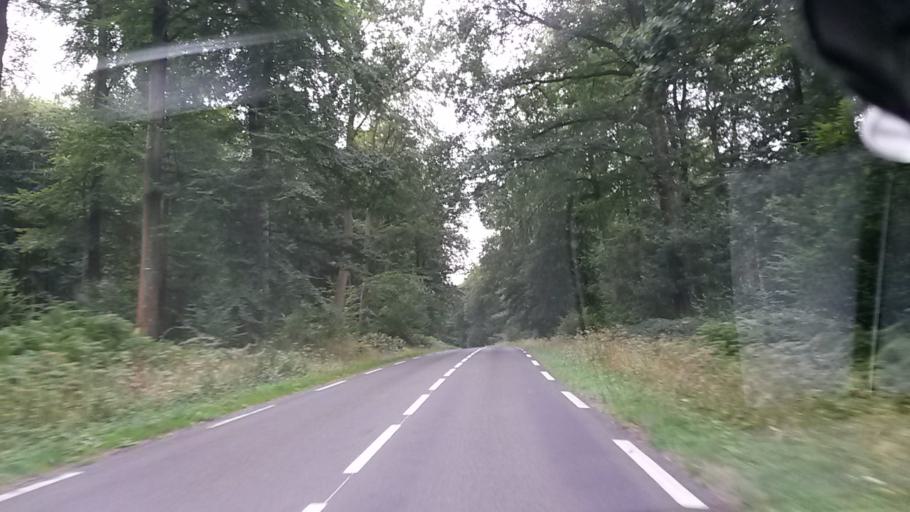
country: FR
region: Haute-Normandie
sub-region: Departement de l'Eure
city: Charleval
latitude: 49.3787
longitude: 1.4671
